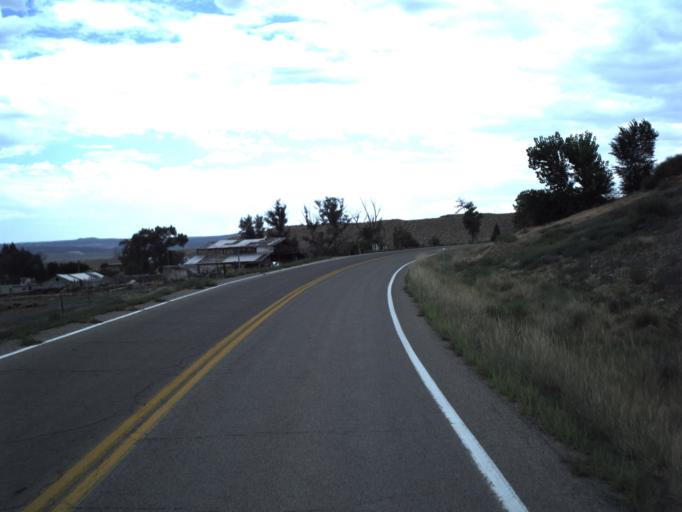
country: US
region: Utah
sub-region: Emery County
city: Huntington
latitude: 39.3699
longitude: -110.8509
